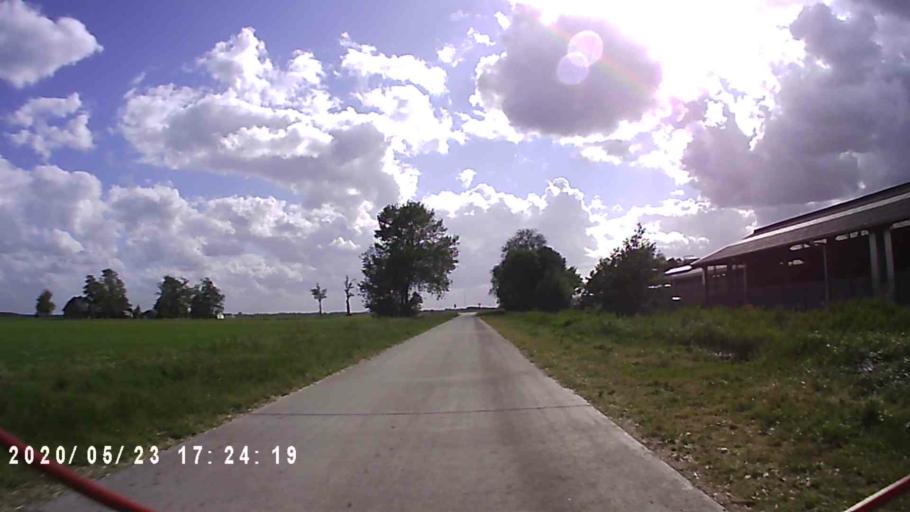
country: NL
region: Groningen
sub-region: Gemeente Slochteren
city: Slochteren
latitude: 53.2569
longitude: 6.7856
